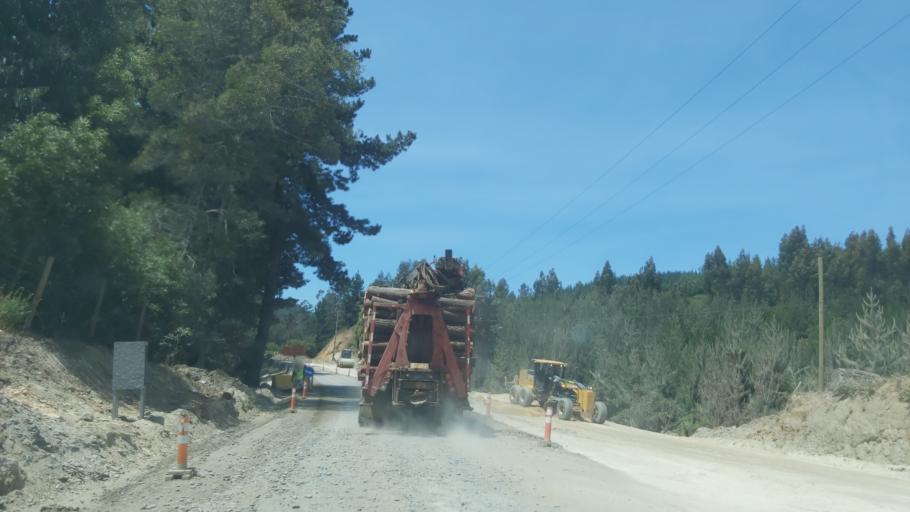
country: CL
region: Maule
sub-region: Provincia de Talca
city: Constitucion
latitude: -35.4485
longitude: -72.4722
